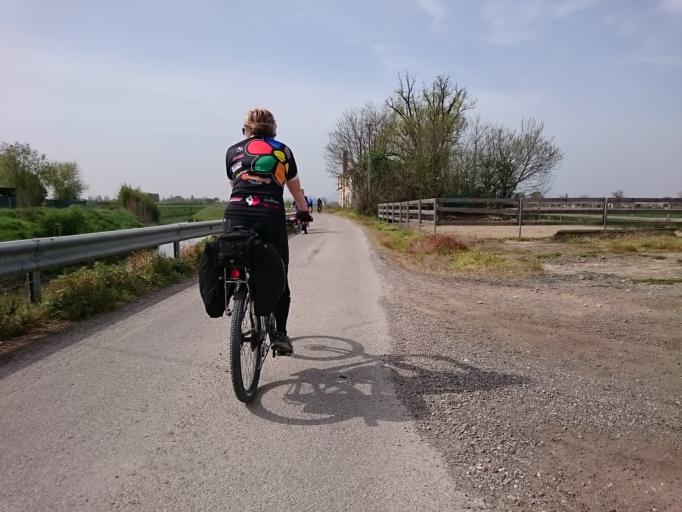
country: IT
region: Veneto
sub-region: Provincia di Padova
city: Tribano
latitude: 45.1874
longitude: 11.8356
